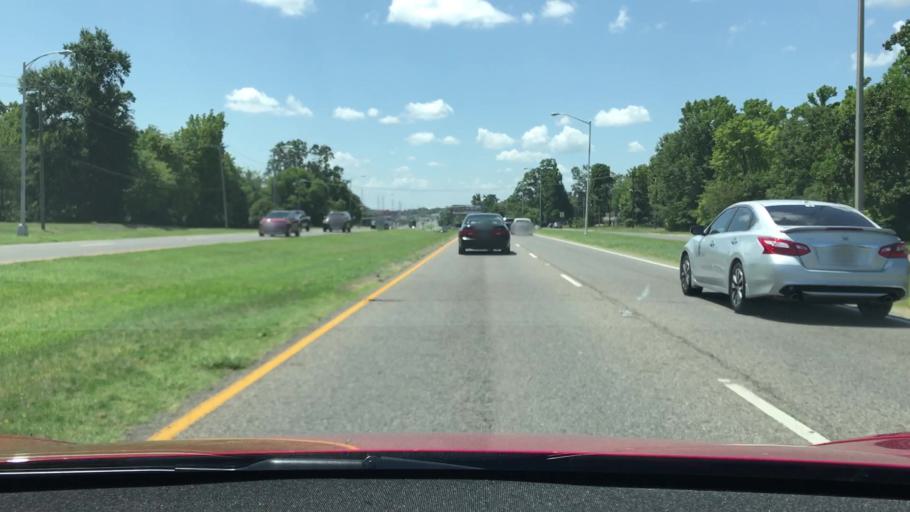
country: US
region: Louisiana
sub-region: Bossier Parish
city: Bossier City
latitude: 32.4961
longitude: -93.7250
